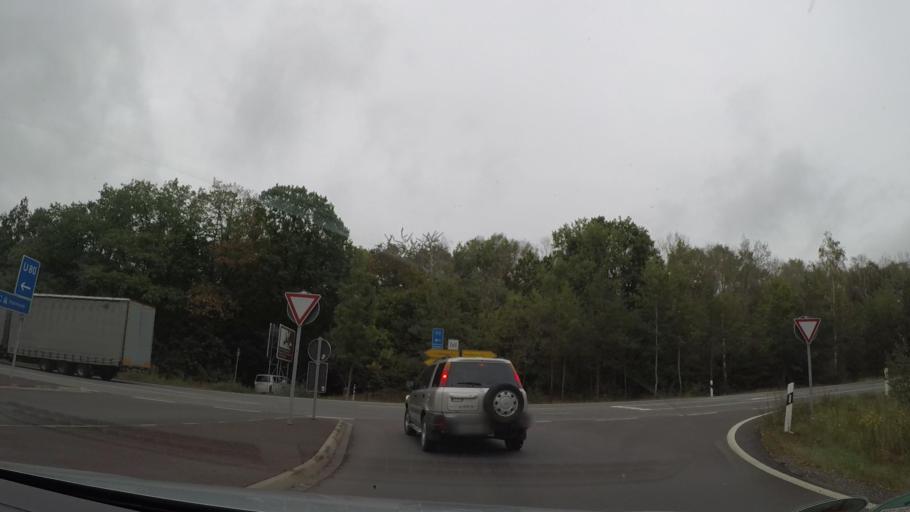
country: DE
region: Saxony-Anhalt
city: Beendorf
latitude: 52.2198
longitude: 11.0755
